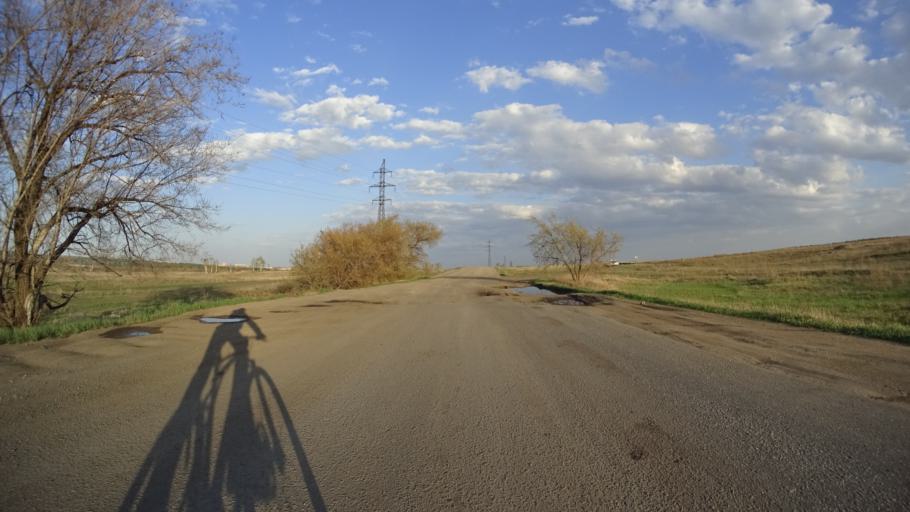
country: RU
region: Chelyabinsk
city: Troitsk
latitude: 54.0533
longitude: 61.5908
